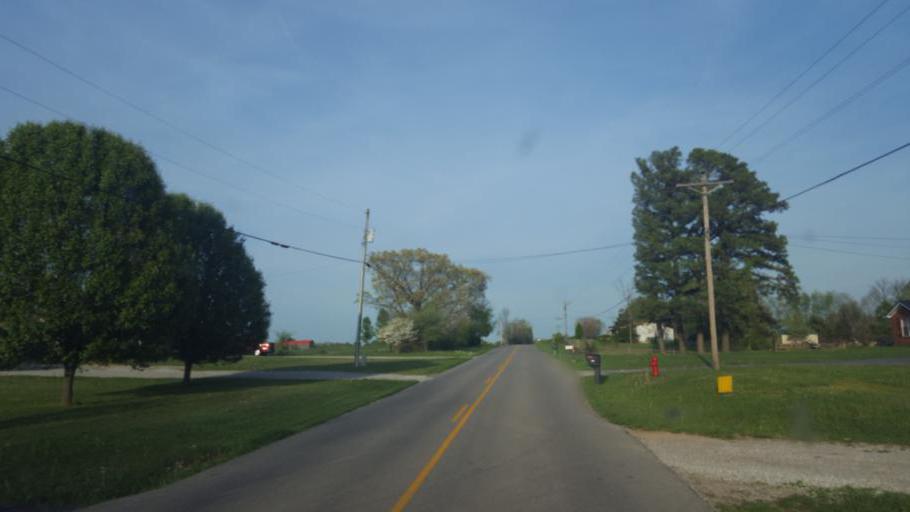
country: US
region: Kentucky
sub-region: Barren County
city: Glasgow
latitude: 36.9457
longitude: -85.9932
